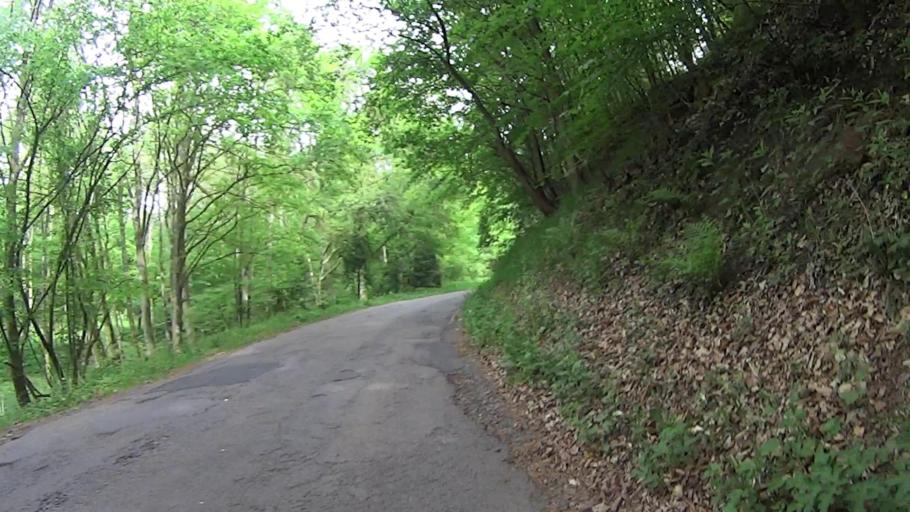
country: BE
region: Wallonia
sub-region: Province de Liege
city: Malmedy
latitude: 50.4437
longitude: 6.0376
